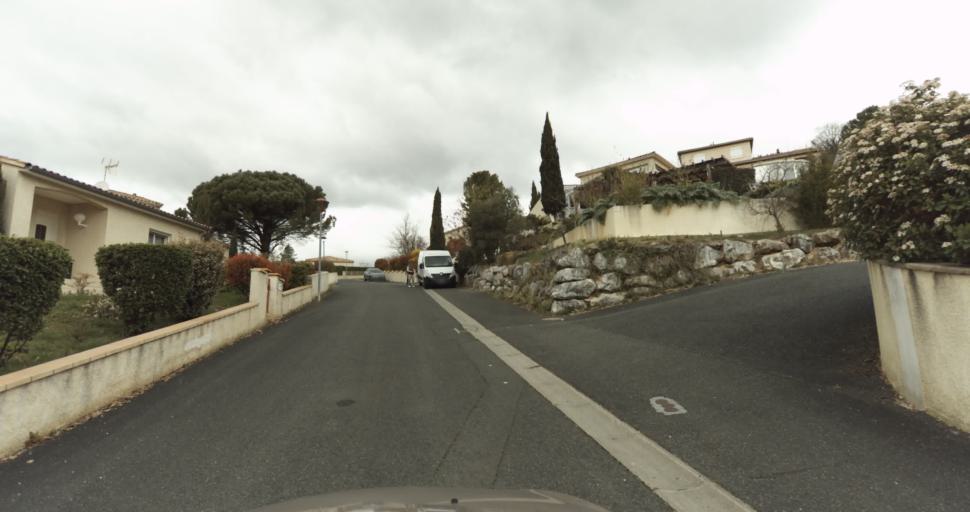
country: FR
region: Midi-Pyrenees
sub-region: Departement du Tarn
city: Puygouzon
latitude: 43.8999
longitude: 2.1630
